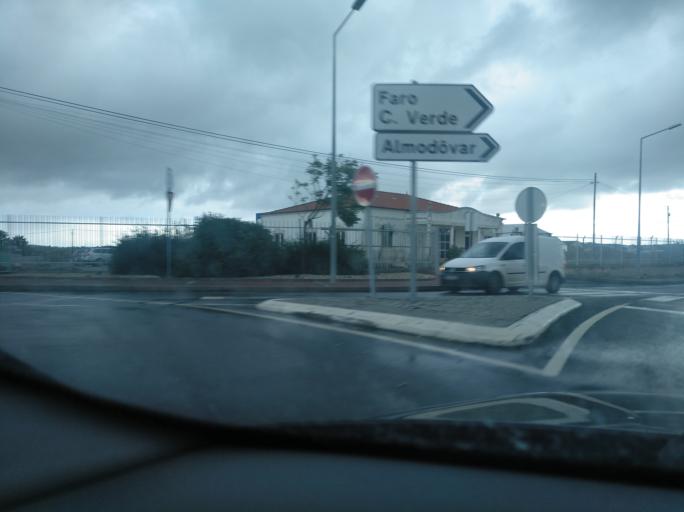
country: PT
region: Beja
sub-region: Aljustrel
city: Aljustrel
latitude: 37.8767
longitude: -8.1528
